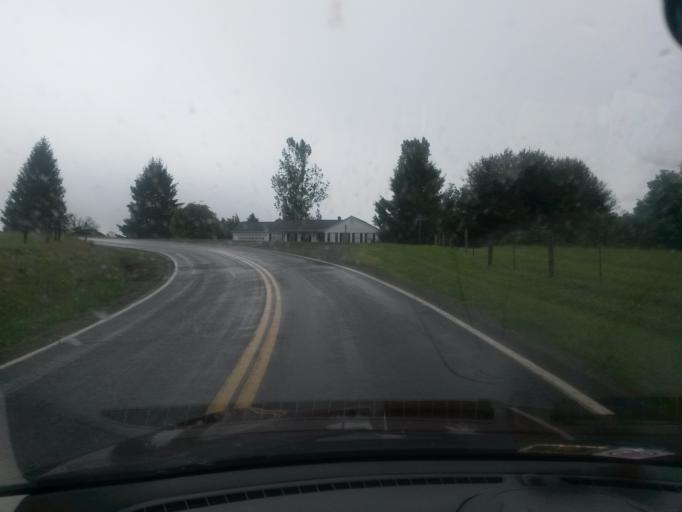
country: US
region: Virginia
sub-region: Patrick County
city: Stuart
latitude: 36.7499
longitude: -80.3933
